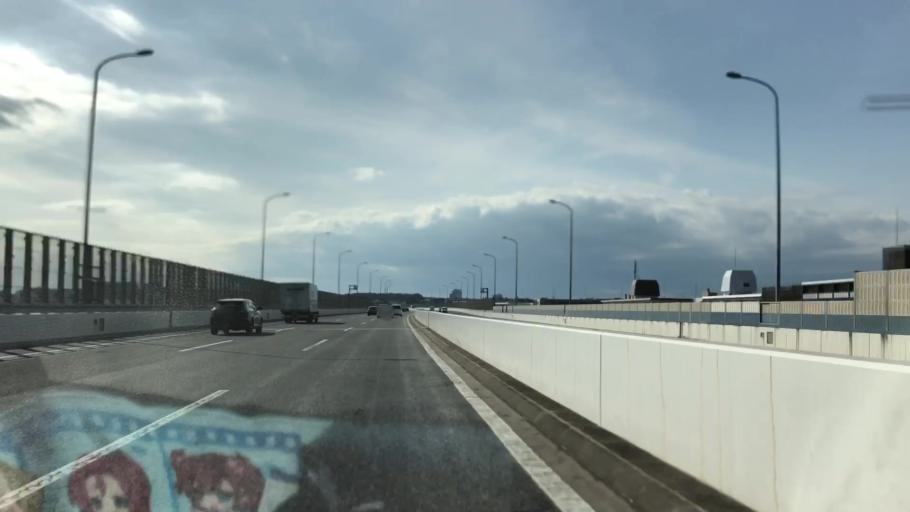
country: JP
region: Kanagawa
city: Yokohama
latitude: 35.4164
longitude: 139.6380
